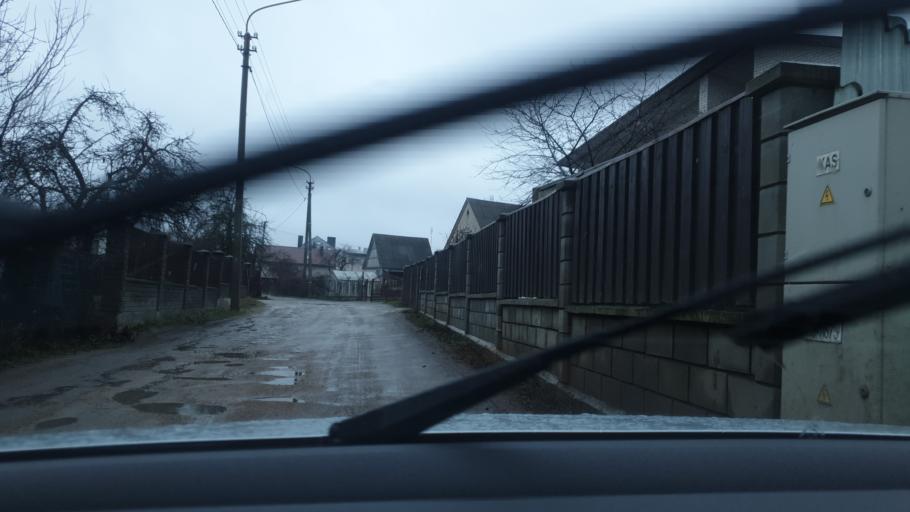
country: LT
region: Vilnius County
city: Rasos
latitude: 54.6633
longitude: 25.3463
